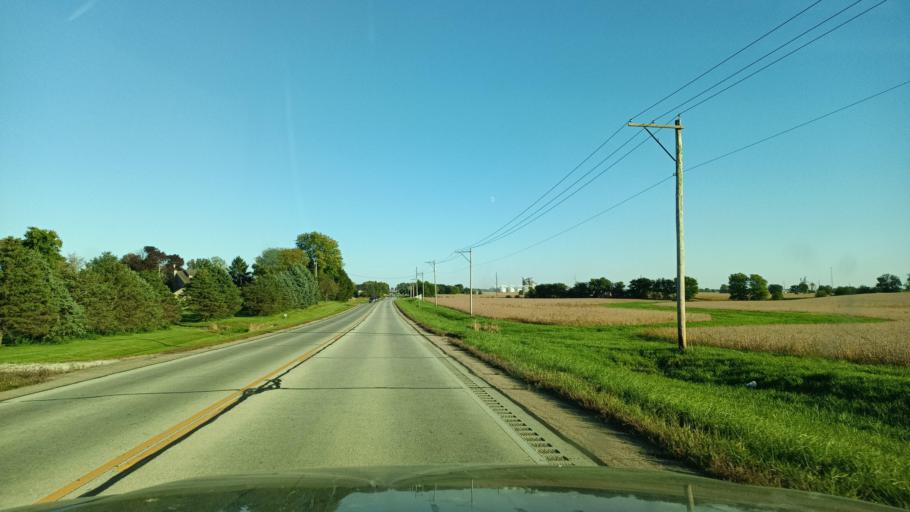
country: US
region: Illinois
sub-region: Champaign County
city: Lake of the Woods
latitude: 40.1743
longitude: -88.3438
